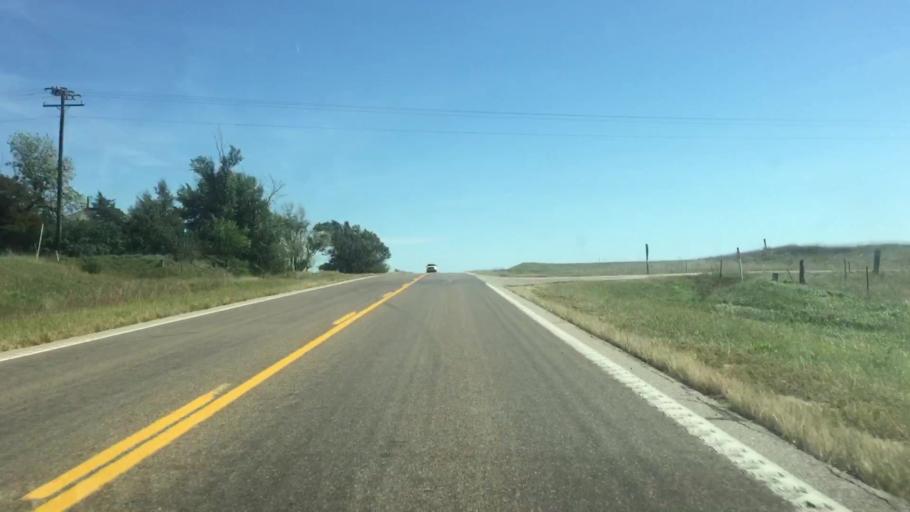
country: US
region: Nebraska
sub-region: Thayer County
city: Hebron
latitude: 40.1472
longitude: -97.5392
